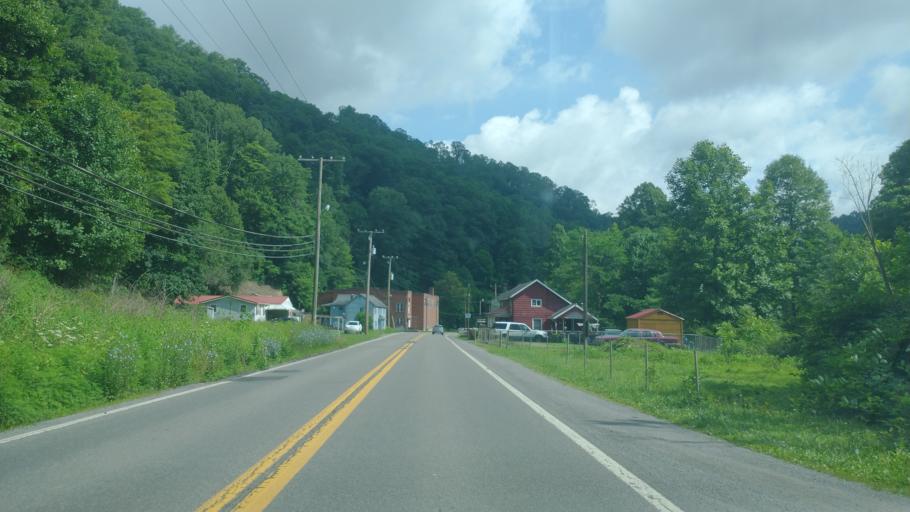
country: US
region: West Virginia
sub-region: McDowell County
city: Welch
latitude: 37.3955
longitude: -81.4224
